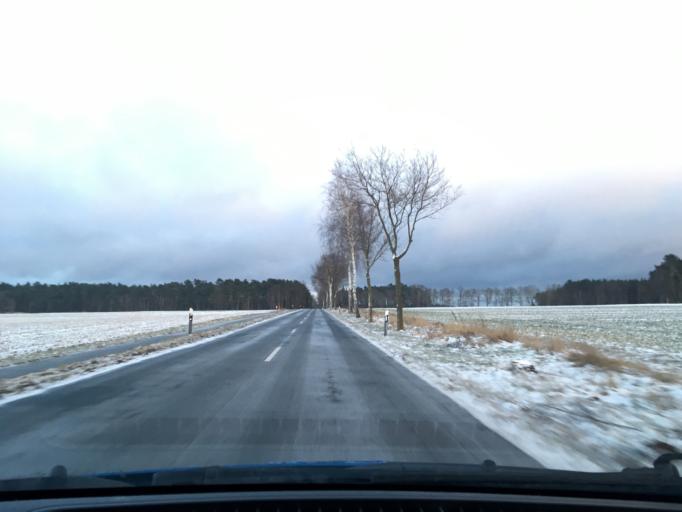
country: DE
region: Lower Saxony
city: Kirchgellersen
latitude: 53.2263
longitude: 10.3127
